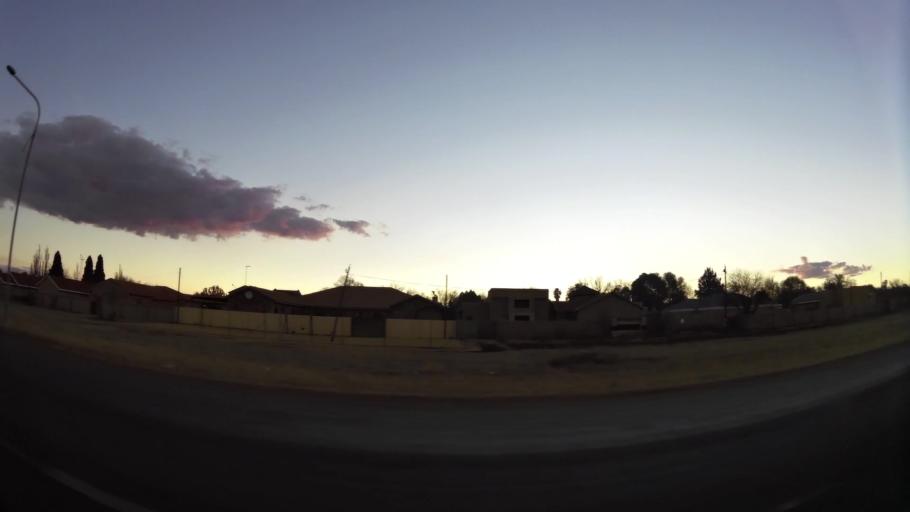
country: ZA
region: North-West
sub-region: Dr Kenneth Kaunda District Municipality
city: Potchefstroom
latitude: -26.6965
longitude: 27.0793
